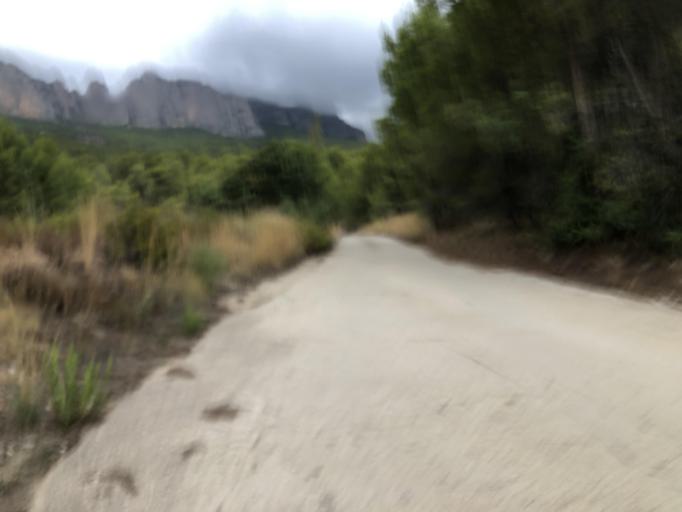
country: ES
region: Valencia
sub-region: Provincia de Alicante
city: Polop
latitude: 38.6369
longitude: -0.1542
